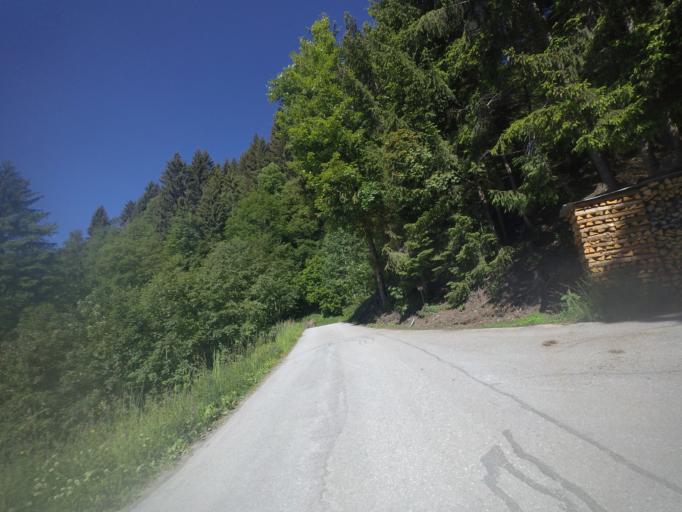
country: AT
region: Salzburg
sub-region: Politischer Bezirk Sankt Johann im Pongau
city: Goldegg
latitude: 47.3313
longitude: 13.0701
